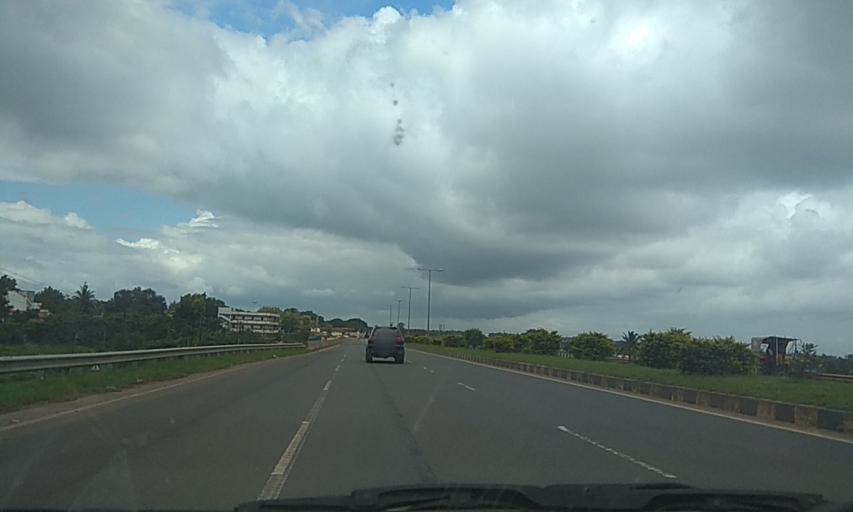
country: IN
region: Karnataka
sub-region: Dharwad
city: Alnavar
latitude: 15.5190
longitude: 74.9184
